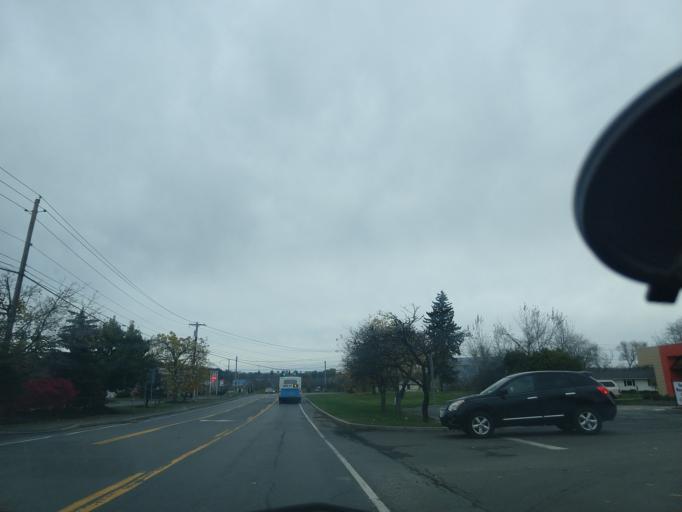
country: US
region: New York
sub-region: Tompkins County
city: East Ithaca
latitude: 42.4376
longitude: -76.4652
